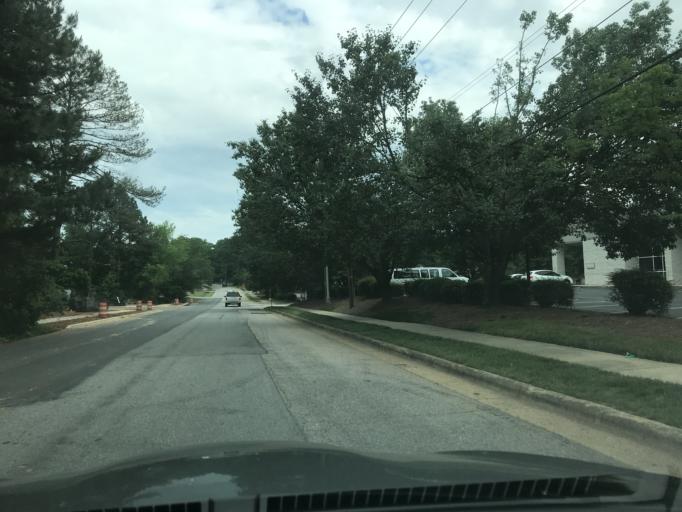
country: US
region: North Carolina
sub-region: Wake County
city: Raleigh
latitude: 35.8640
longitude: -78.5905
